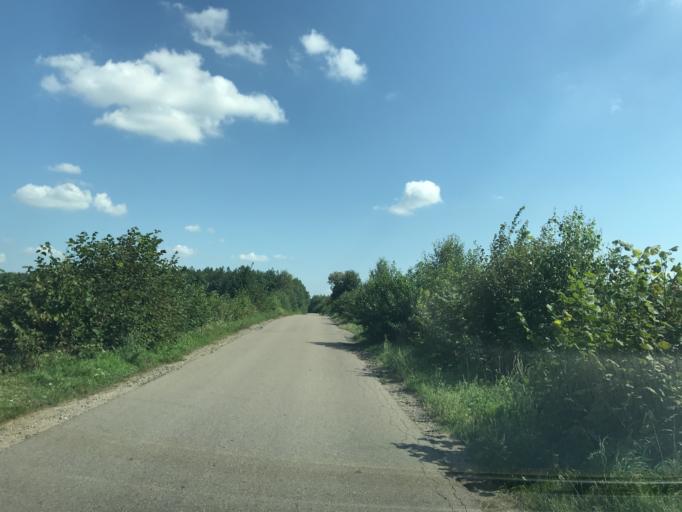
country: PL
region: Masovian Voivodeship
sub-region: Powiat zurominski
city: Lubowidz
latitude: 53.1599
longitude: 19.9072
